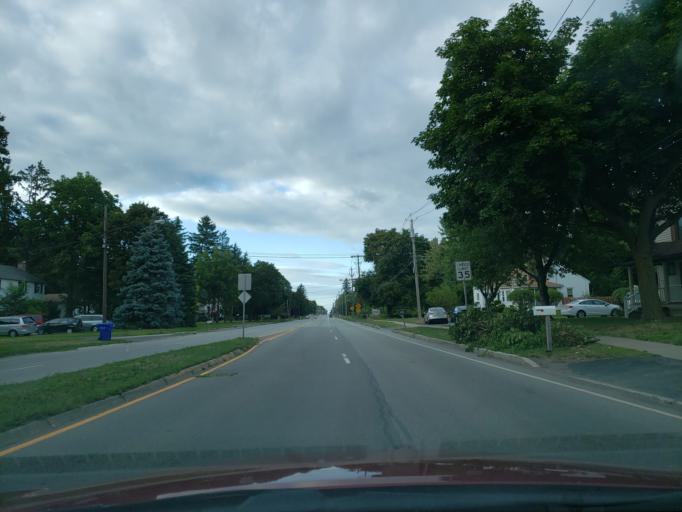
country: US
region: New York
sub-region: Monroe County
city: Greece
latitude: 43.2162
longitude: -77.6589
